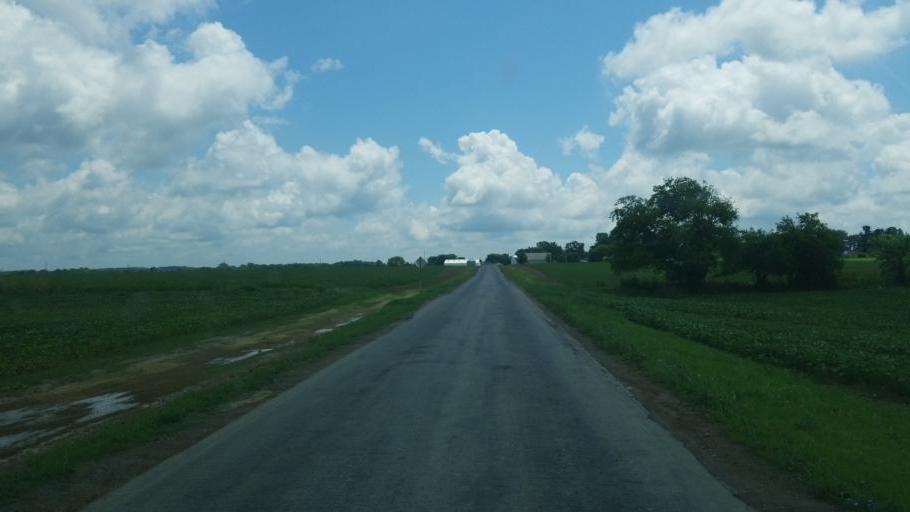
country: US
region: Ohio
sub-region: Highland County
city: Greenfield
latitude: 39.2659
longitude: -83.4503
